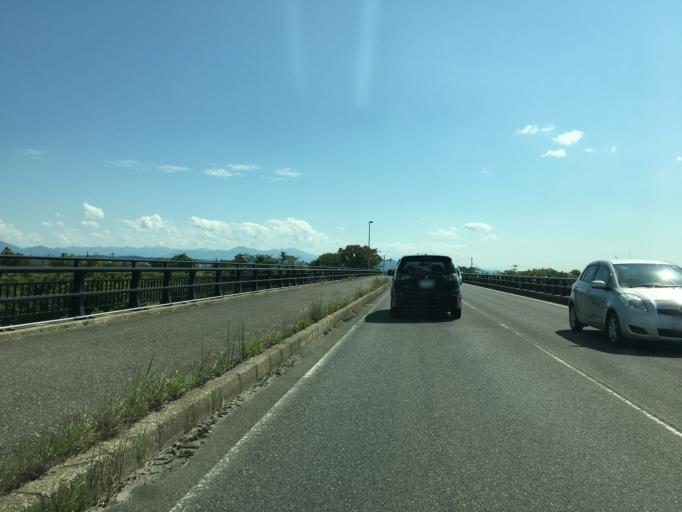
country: JP
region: Niigata
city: Kameda-honcho
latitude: 37.8368
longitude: 139.0963
